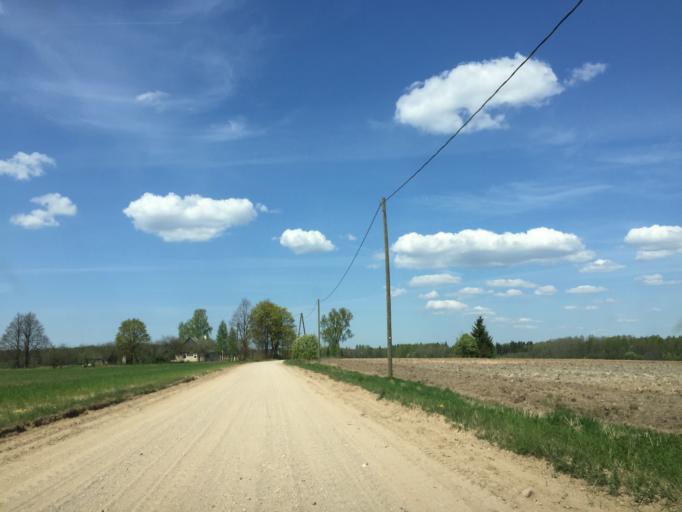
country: LV
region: Limbazu Rajons
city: Limbazi
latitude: 57.3525
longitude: 24.6487
